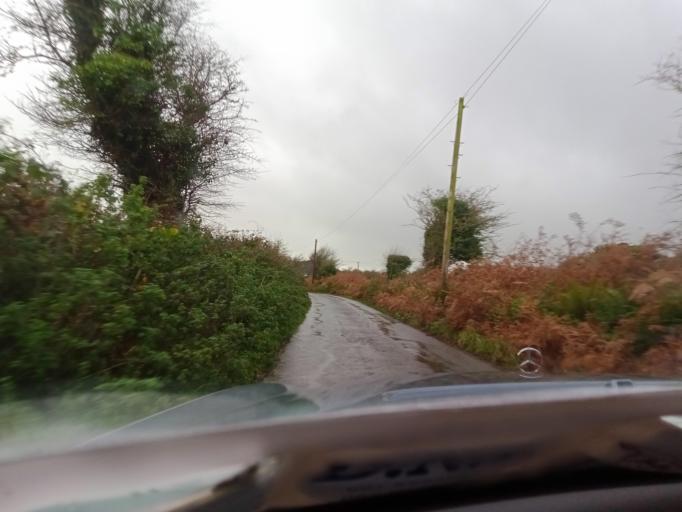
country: IE
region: Leinster
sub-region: Kilkenny
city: Mooncoin
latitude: 52.2594
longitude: -7.2012
